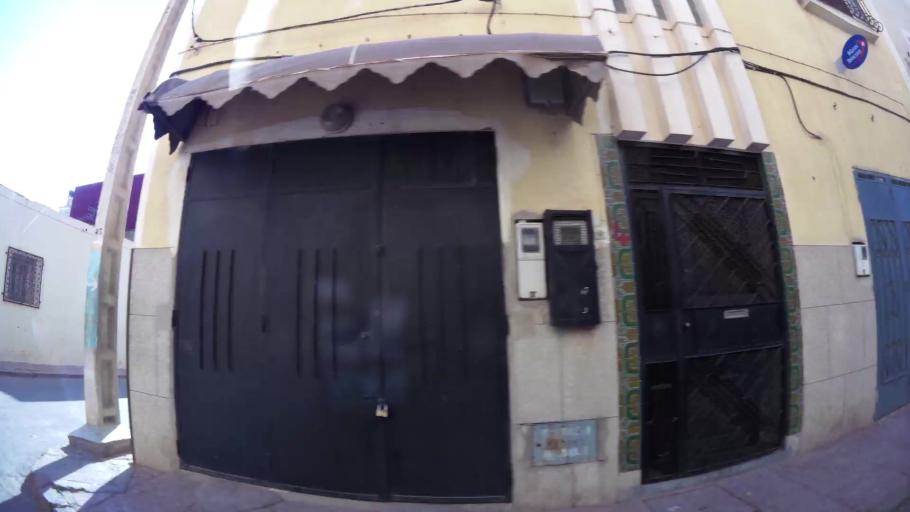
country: MA
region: Oriental
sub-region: Oujda-Angad
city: Oujda
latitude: 34.6795
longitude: -1.9295
